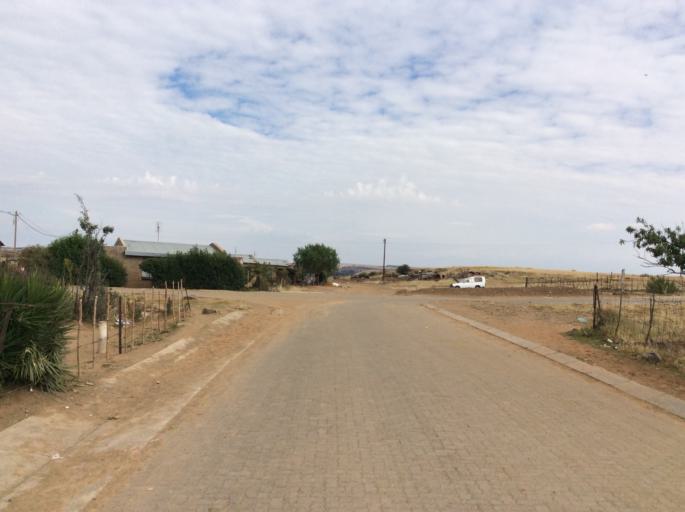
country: LS
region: Mafeteng
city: Mafeteng
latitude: -29.7175
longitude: 27.0121
